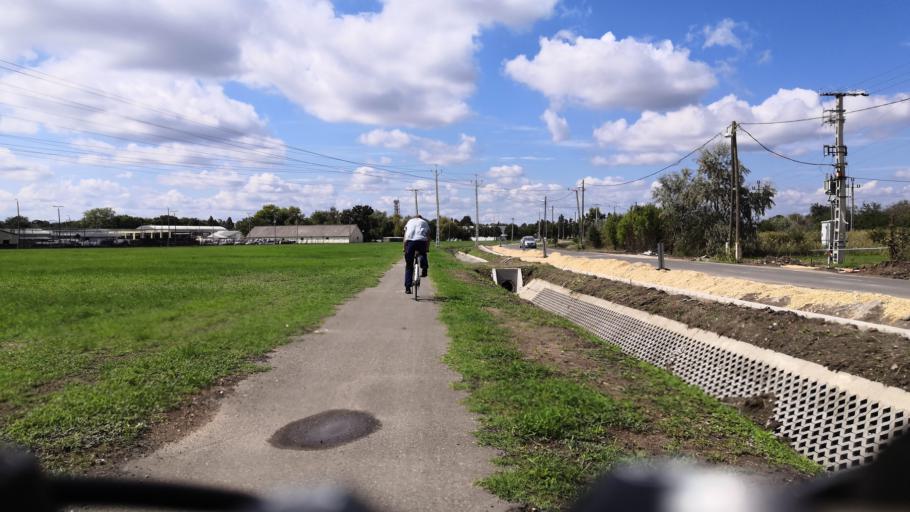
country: HU
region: Csongrad
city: Szeged
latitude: 46.2779
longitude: 20.1339
